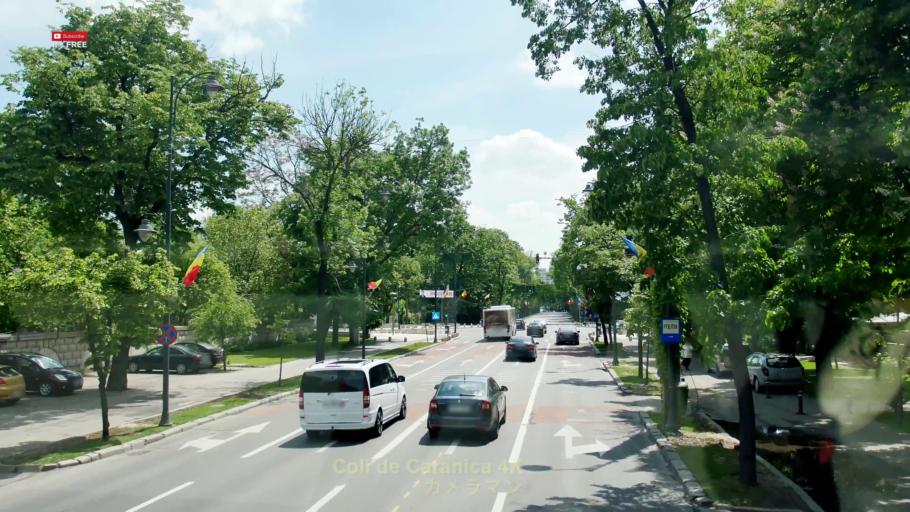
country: RO
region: Bucuresti
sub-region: Municipiul Bucuresti
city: Bucuresti
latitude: 44.4600
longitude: 26.0817
